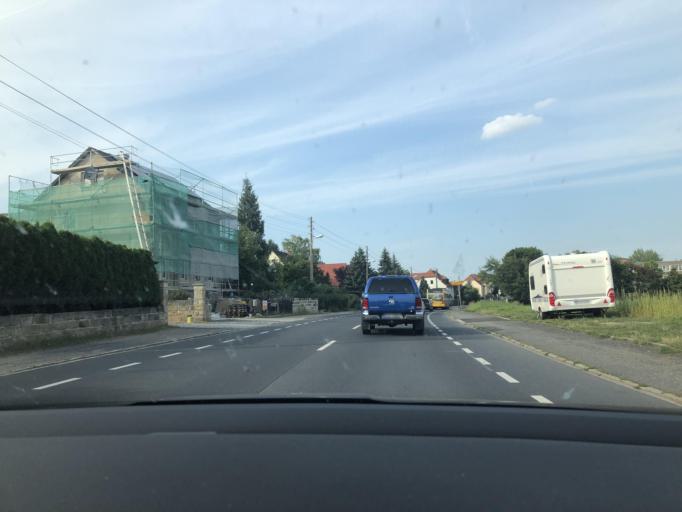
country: DE
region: Saxony
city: Albertstadt
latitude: 51.1149
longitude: 13.7280
